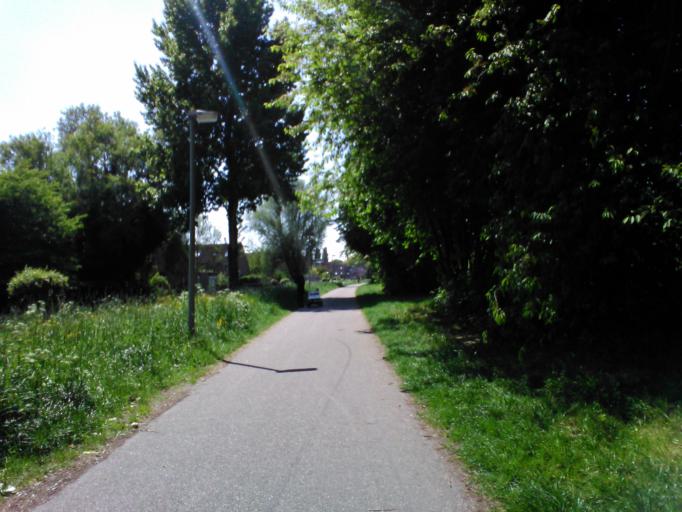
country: NL
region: South Holland
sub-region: Gemeente Sliedrecht
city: Sliedrecht
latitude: 51.8023
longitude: 4.7304
